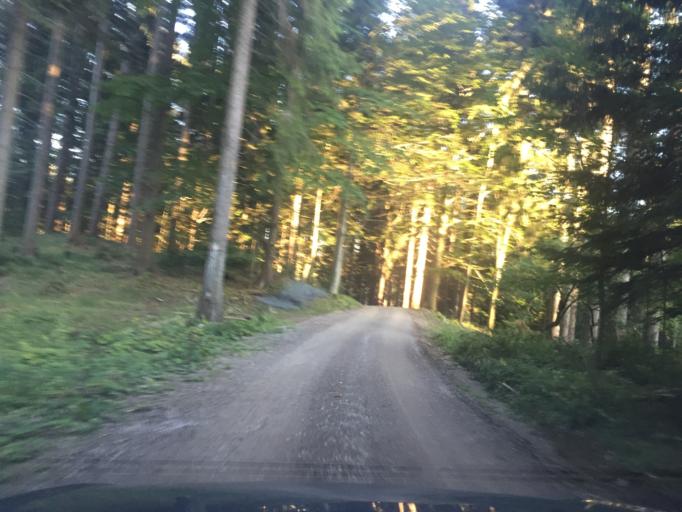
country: SI
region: Ravne na Koroskem
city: Kotlje
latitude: 46.4774
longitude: 14.9816
